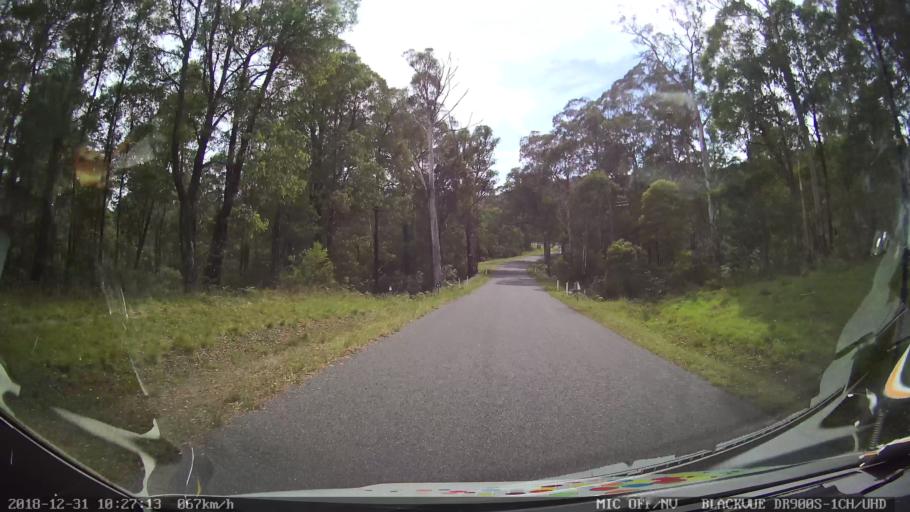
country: AU
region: New South Wales
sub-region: Snowy River
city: Jindabyne
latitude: -36.4878
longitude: 148.1421
